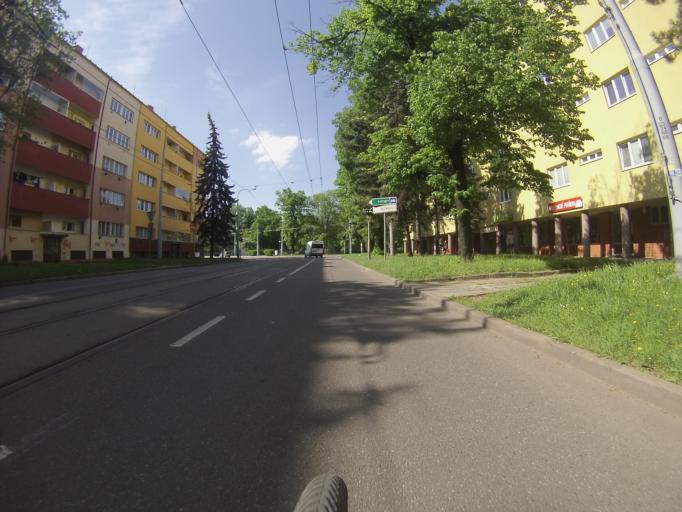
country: CZ
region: South Moravian
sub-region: Mesto Brno
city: Brno
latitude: 49.2128
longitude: 16.5927
